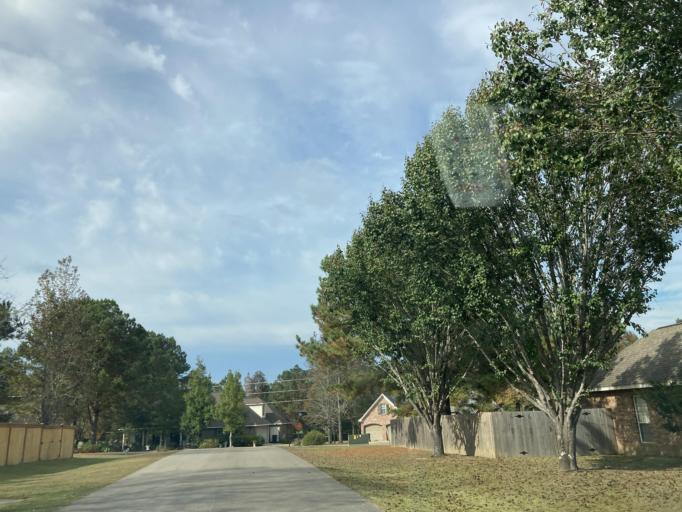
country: US
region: Mississippi
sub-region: Lamar County
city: West Hattiesburg
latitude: 31.3324
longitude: -89.4337
